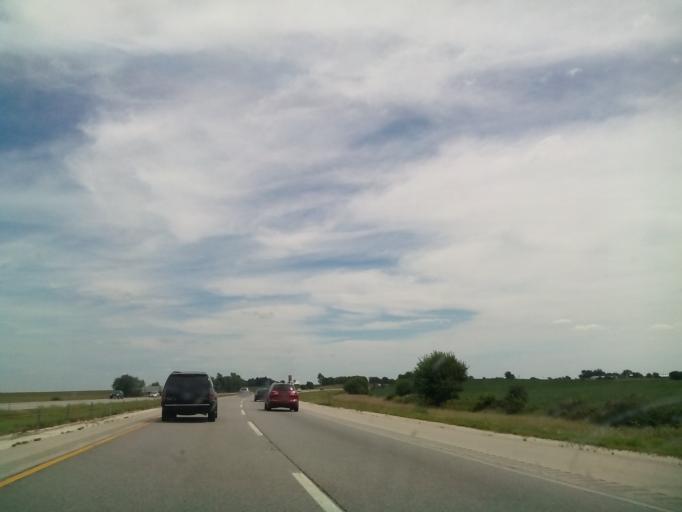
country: US
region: Illinois
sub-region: DeKalb County
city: Cortland
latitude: 41.9009
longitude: -88.6525
